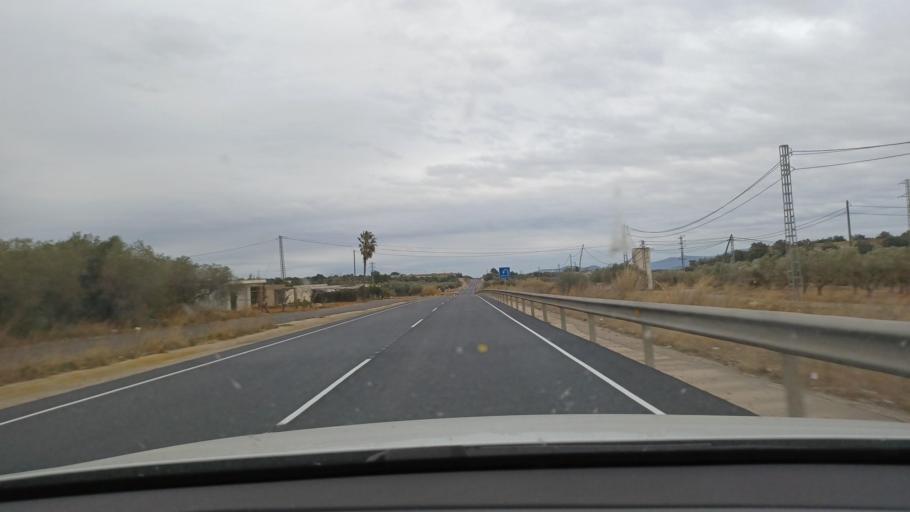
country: ES
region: Valencia
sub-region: Provincia de Castello
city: Traiguera
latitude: 40.5399
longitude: 0.3116
